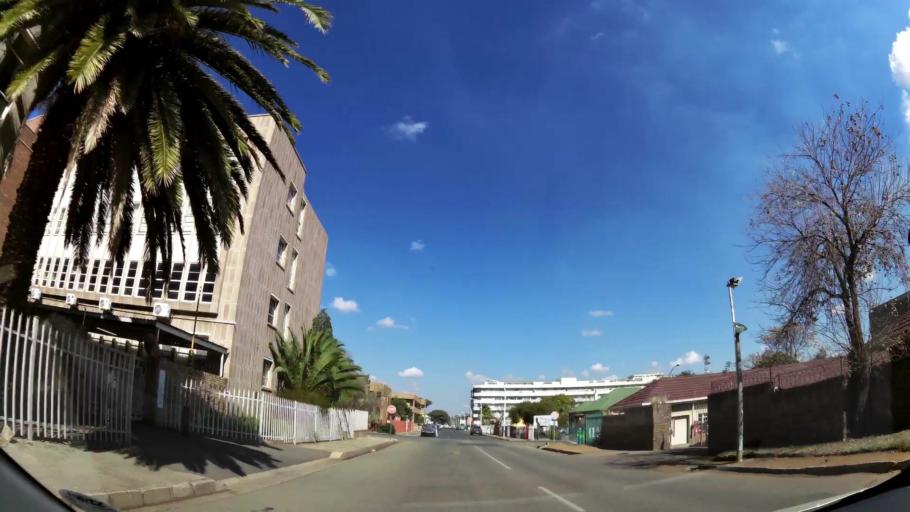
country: ZA
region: Mpumalanga
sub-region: Nkangala District Municipality
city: Witbank
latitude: -25.8734
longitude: 29.2173
